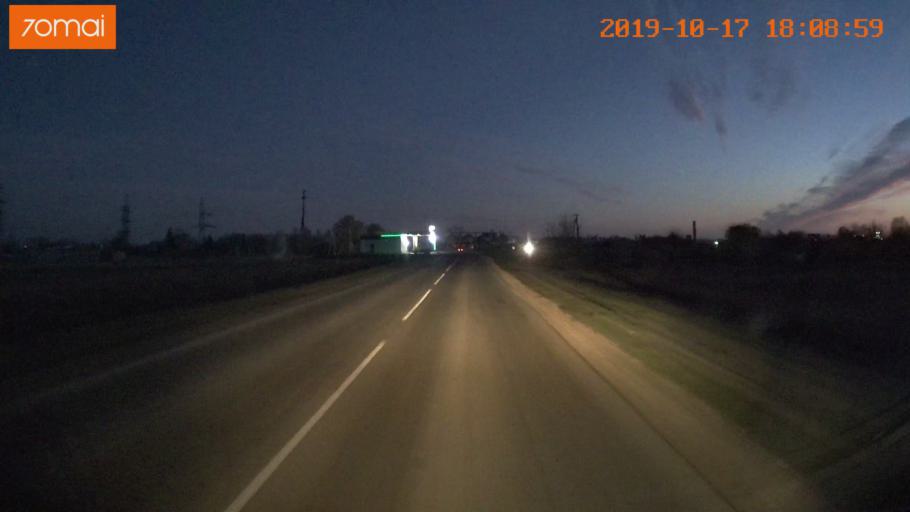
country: RU
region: Tula
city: Kurkino
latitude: 53.4274
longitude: 38.6448
